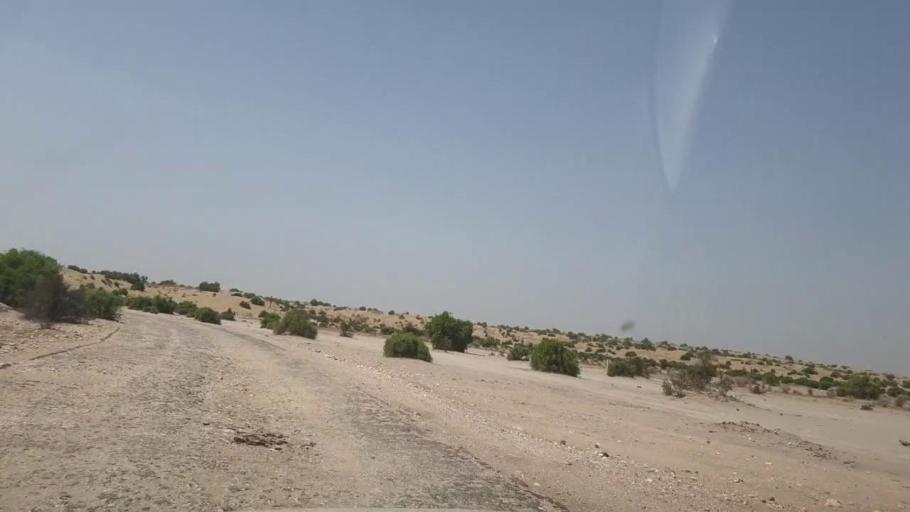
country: PK
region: Sindh
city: Khanpur
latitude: 27.3637
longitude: 69.3146
